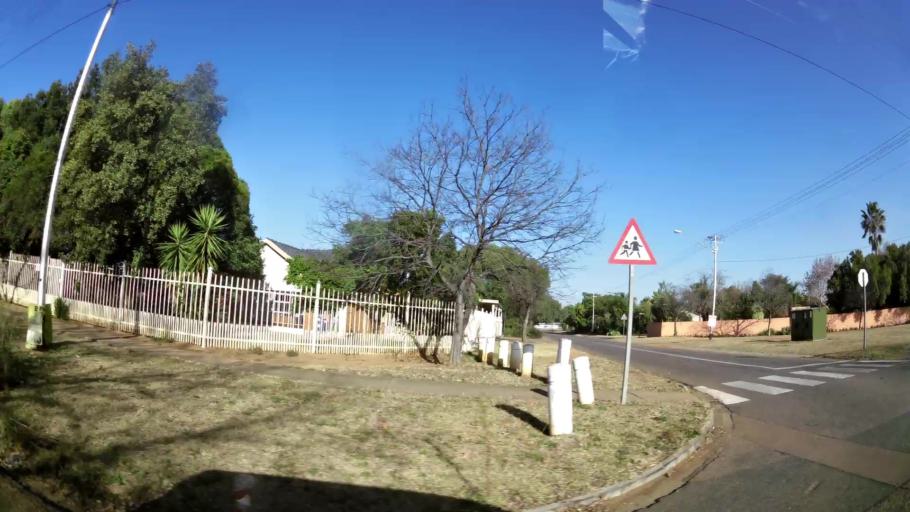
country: ZA
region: Gauteng
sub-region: City of Tshwane Metropolitan Municipality
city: Pretoria
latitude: -25.7113
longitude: 28.2555
